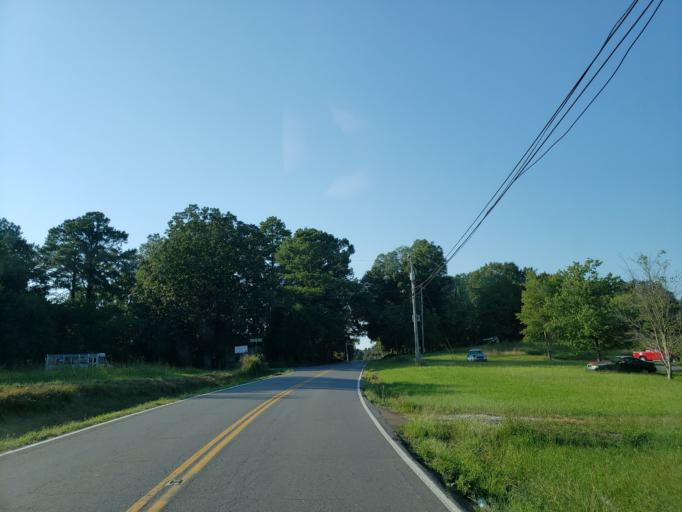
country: US
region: Tennessee
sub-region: Bradley County
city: Wildwood Lake
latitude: 35.0767
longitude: -84.7852
